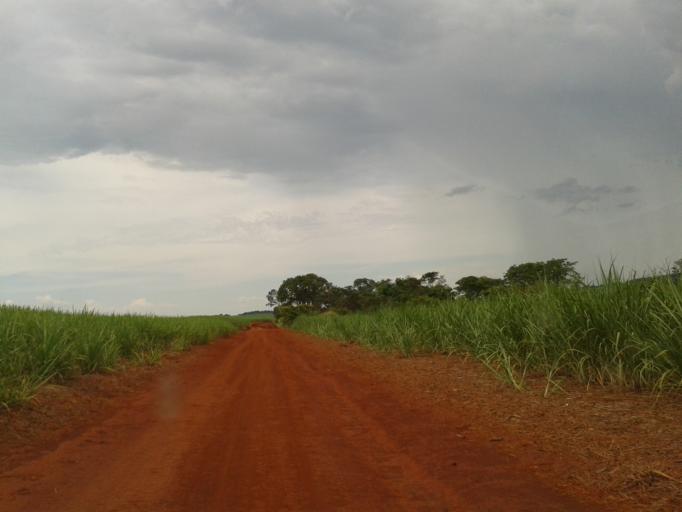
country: BR
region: Minas Gerais
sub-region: Centralina
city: Centralina
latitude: -18.6652
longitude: -49.2393
